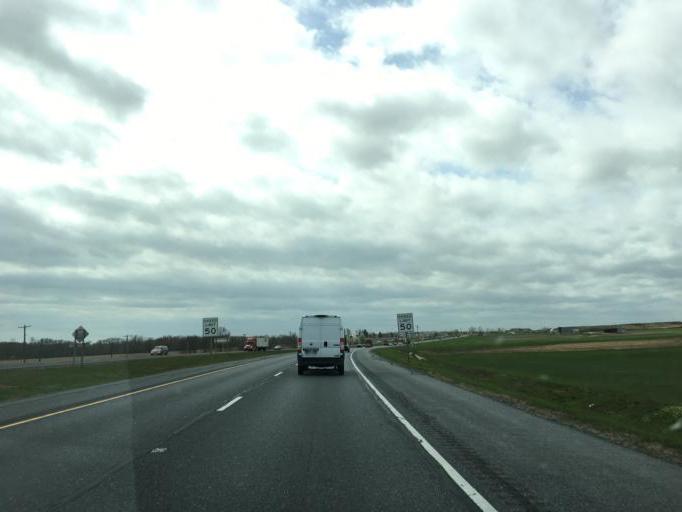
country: US
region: Maryland
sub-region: Frederick County
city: Clover Hill
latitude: 39.4801
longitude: -77.3971
